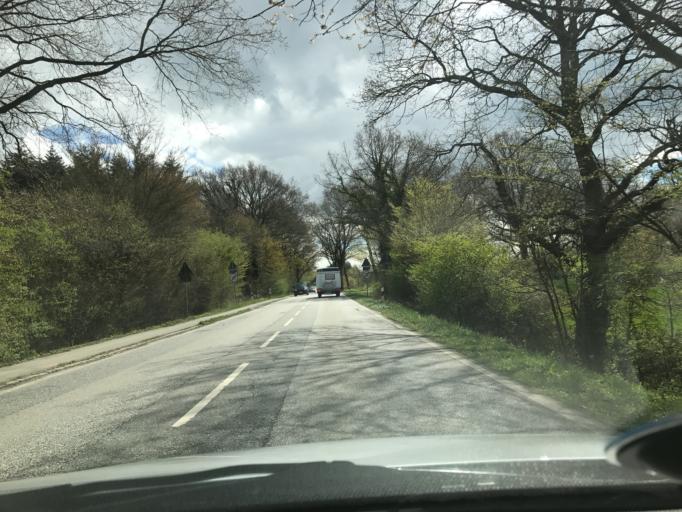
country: DE
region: Schleswig-Holstein
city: Susel
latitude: 54.0915
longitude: 10.6820
